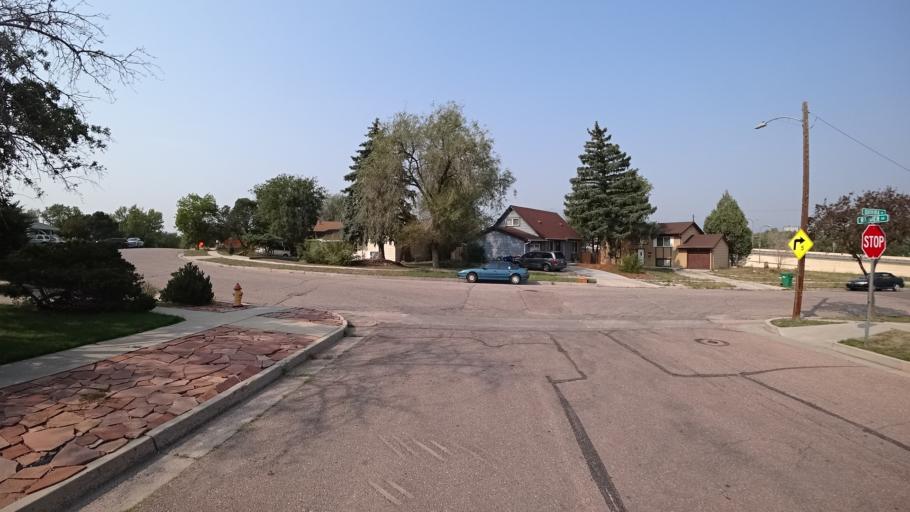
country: US
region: Colorado
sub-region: El Paso County
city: Stratmoor
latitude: 38.8170
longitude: -104.7763
